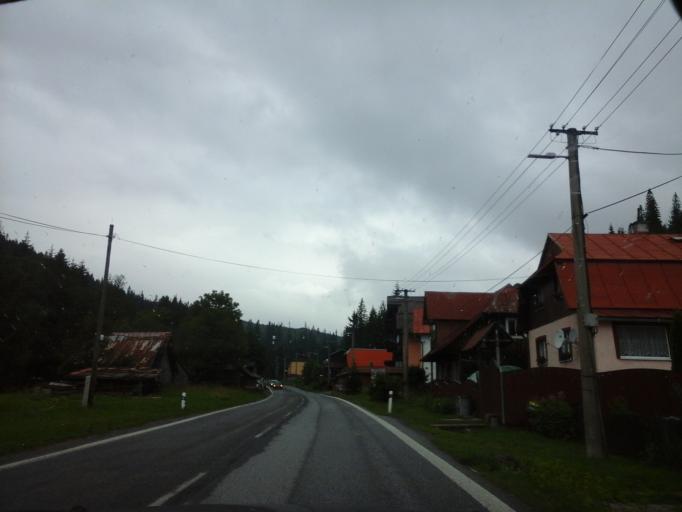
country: SK
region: Presovsky
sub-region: Okres Poprad
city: Zdiar
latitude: 49.2667
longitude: 20.2905
